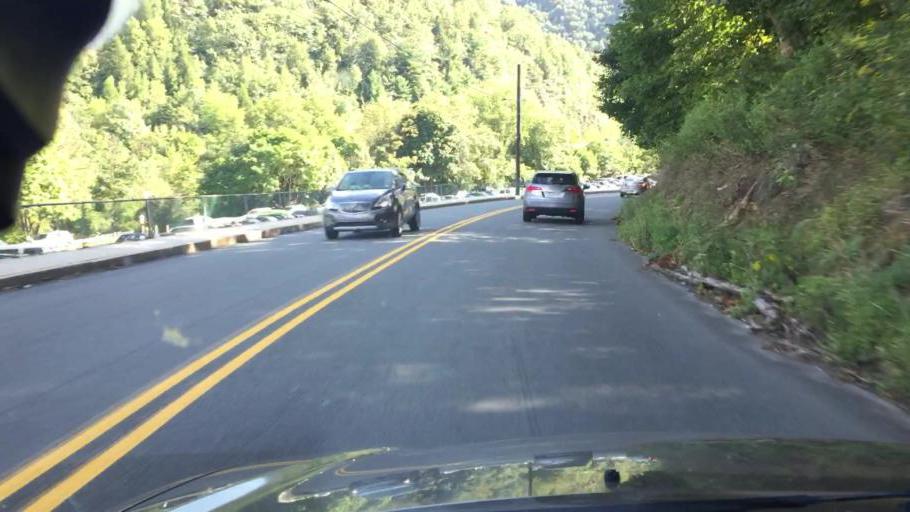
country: US
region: Pennsylvania
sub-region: Carbon County
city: Jim Thorpe
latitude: 40.8658
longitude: -75.7359
